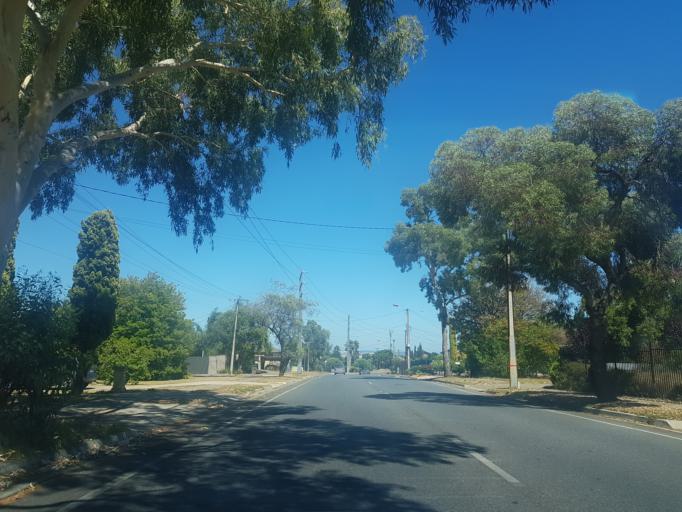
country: AU
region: South Australia
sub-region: Tea Tree Gully
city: Modbury
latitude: -34.8188
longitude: 138.6658
